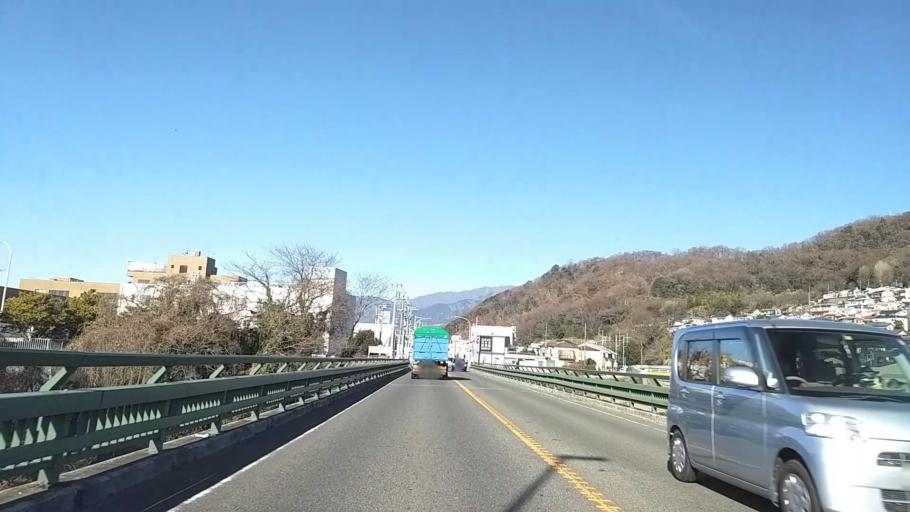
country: JP
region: Kanagawa
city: Hadano
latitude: 35.3642
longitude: 139.2451
